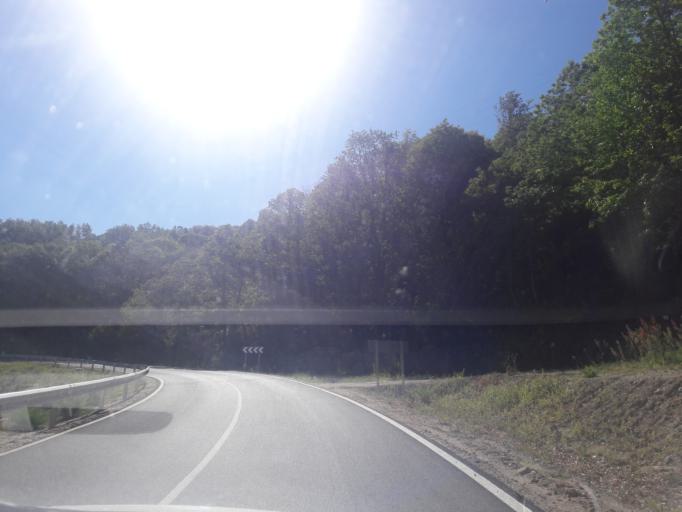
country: ES
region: Castille and Leon
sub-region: Provincia de Salamanca
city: Montemayor del Rio
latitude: 40.3347
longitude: -5.8992
